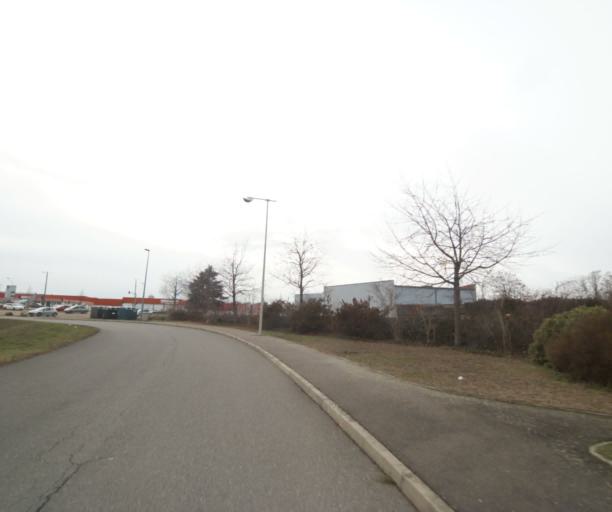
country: FR
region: Rhone-Alpes
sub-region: Departement de la Loire
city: Le Coteau
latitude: 46.0526
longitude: 4.0870
